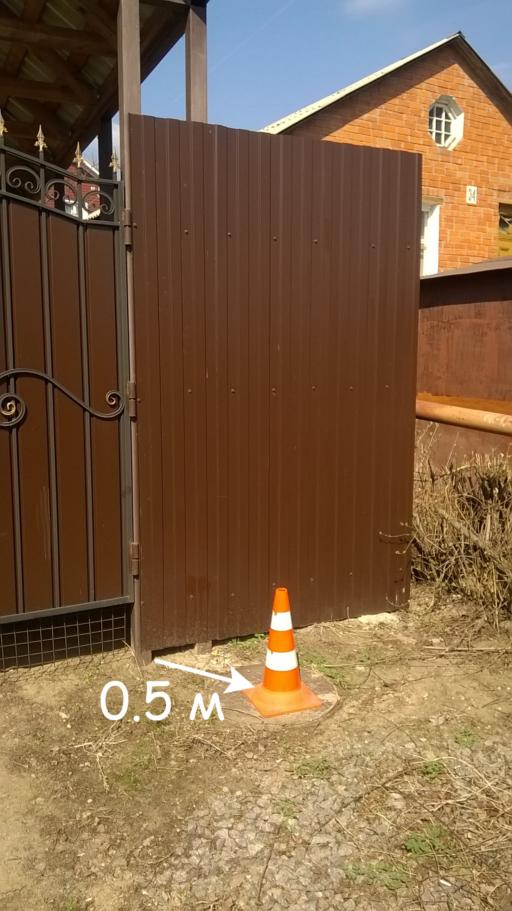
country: RU
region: Voronezj
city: Voronezh
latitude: 51.7002
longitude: 39.2336
